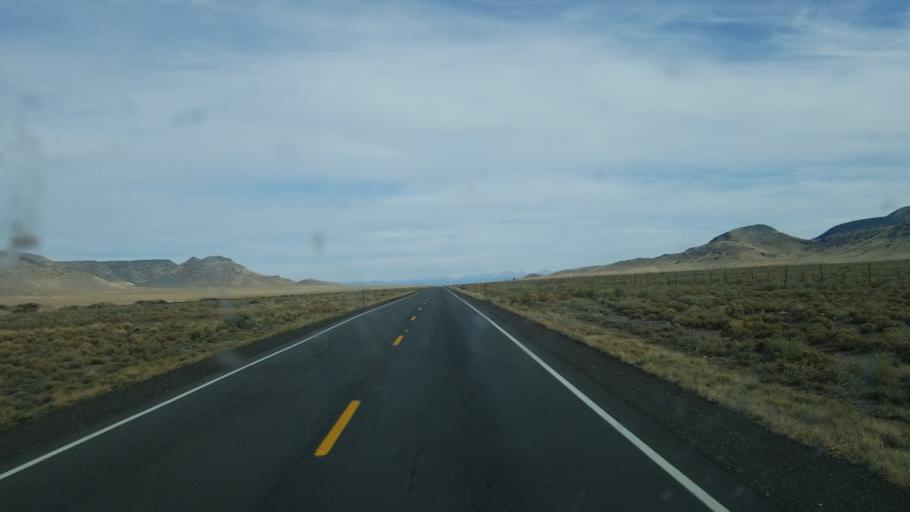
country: US
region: Colorado
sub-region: Conejos County
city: Conejos
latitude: 37.1754
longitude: -105.8640
